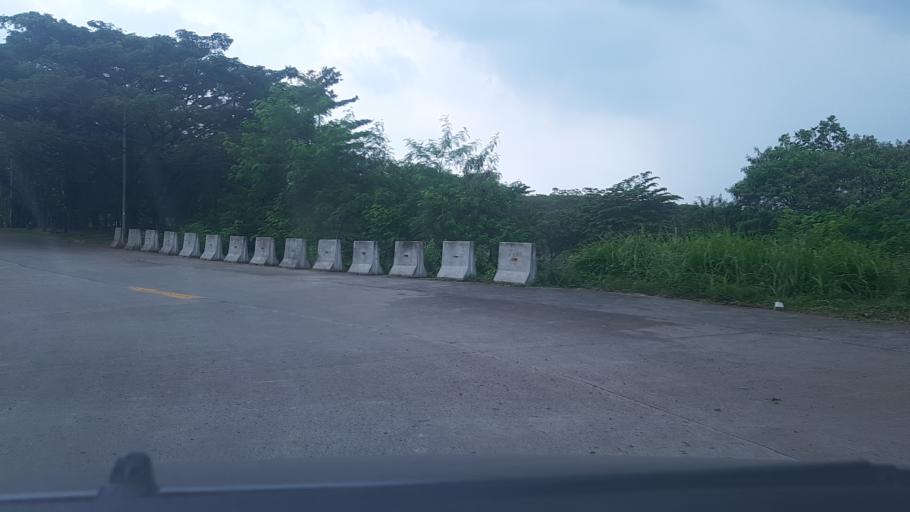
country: ID
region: West Java
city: Citeureup
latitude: -6.5734
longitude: 106.8907
